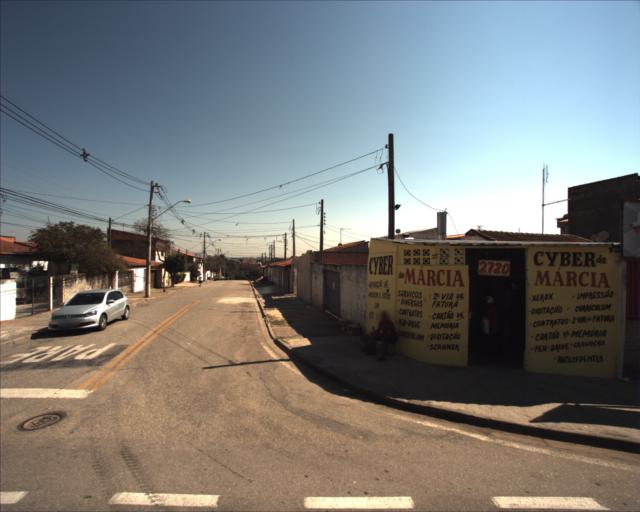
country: BR
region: Sao Paulo
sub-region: Sorocaba
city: Sorocaba
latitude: -23.5031
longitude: -47.5113
